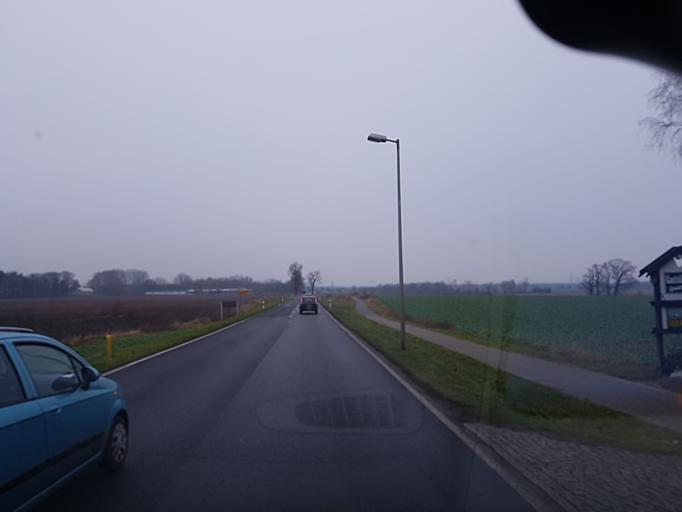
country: DE
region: Brandenburg
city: Lubbenau
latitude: 51.8710
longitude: 13.9158
